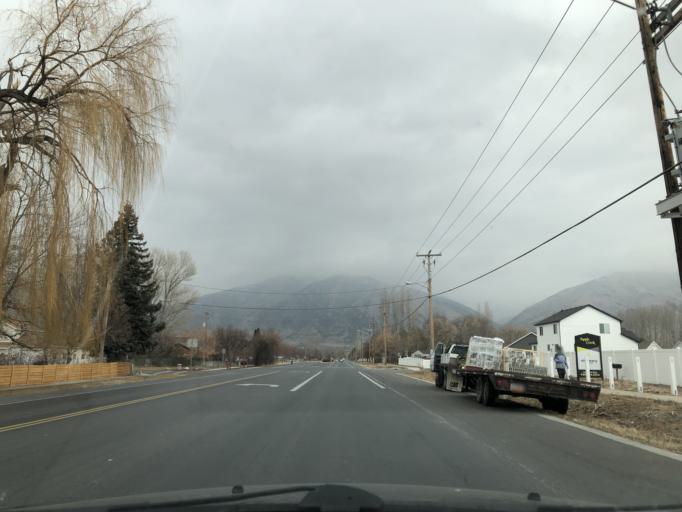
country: US
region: Utah
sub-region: Cache County
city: Nibley
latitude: 41.6748
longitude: -111.8458
